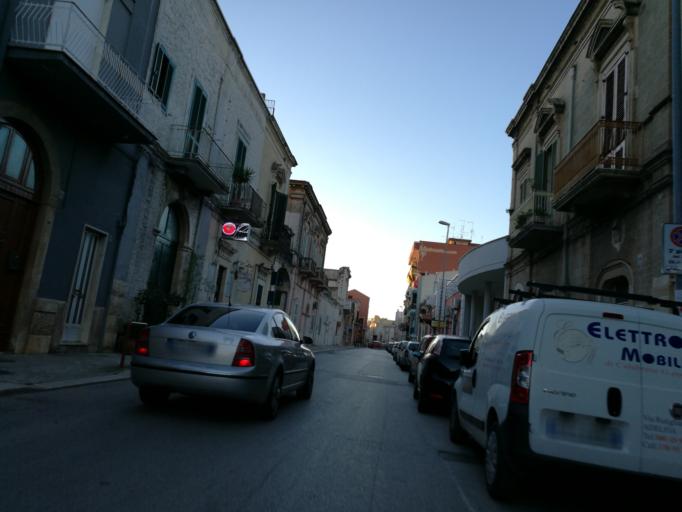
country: IT
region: Apulia
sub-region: Provincia di Bari
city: Adelfia
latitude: 41.0042
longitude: 16.8789
